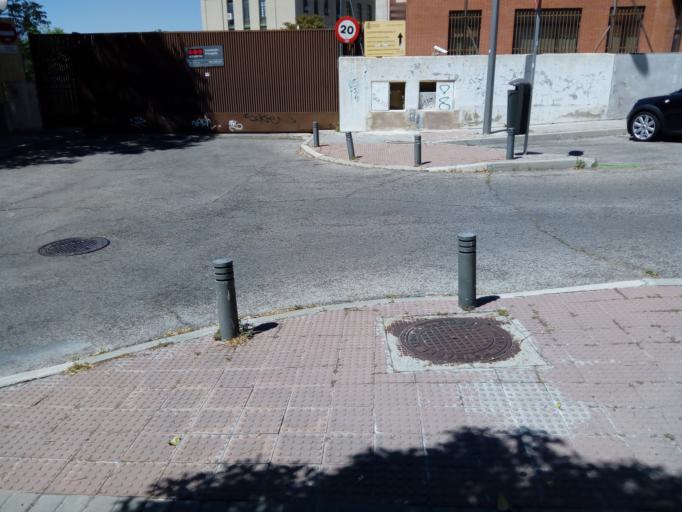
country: ES
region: Madrid
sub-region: Provincia de Madrid
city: Retiro
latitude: 40.4075
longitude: -3.6848
